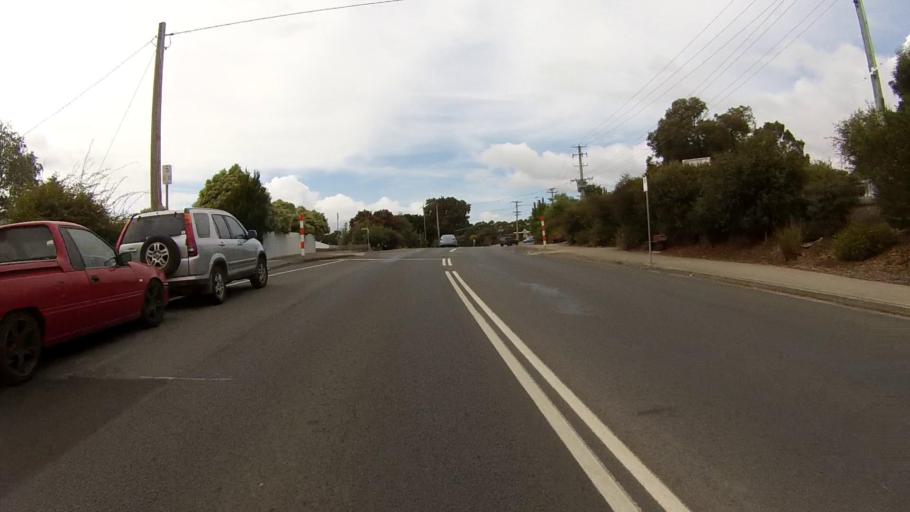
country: AU
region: Tasmania
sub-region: Kingborough
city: Margate
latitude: -43.0275
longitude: 147.2624
